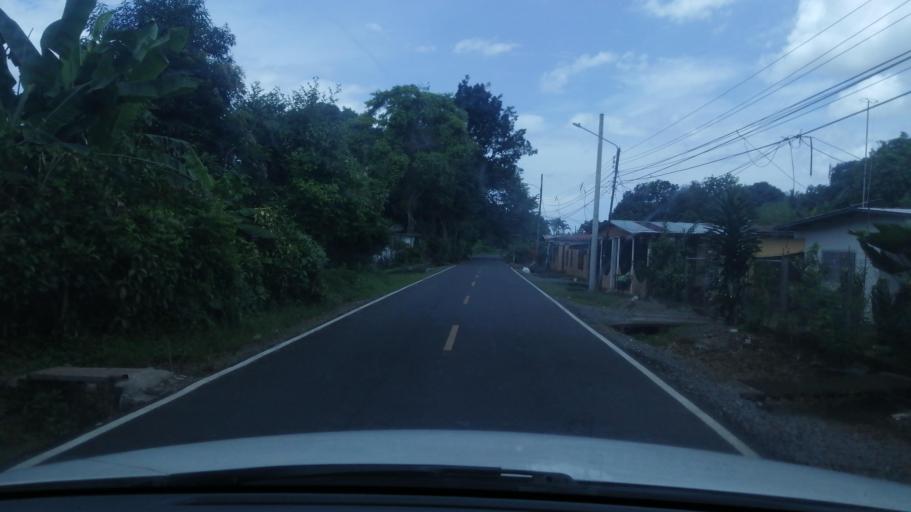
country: PA
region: Chiriqui
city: David
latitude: 8.4129
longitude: -82.4270
